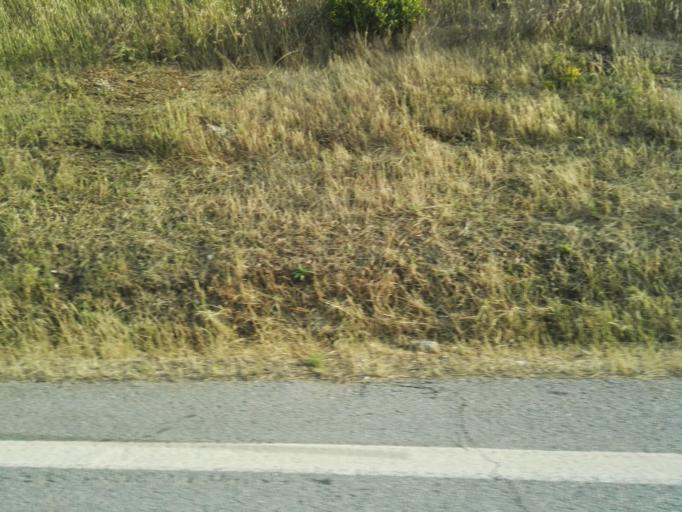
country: PT
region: Portalegre
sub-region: Elvas
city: Elvas
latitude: 38.8745
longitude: -7.1582
